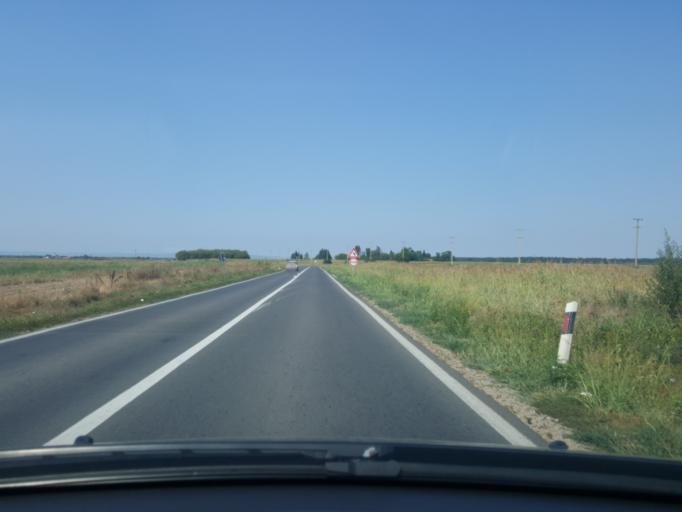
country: RS
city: Hrtkovci
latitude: 44.8493
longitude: 19.7698
